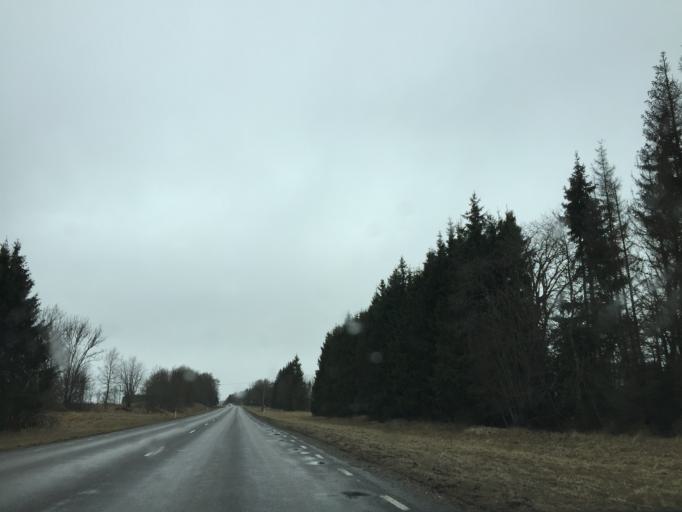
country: EE
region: Laeaene
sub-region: Ridala Parish
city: Uuemoisa
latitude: 58.8759
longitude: 23.6111
